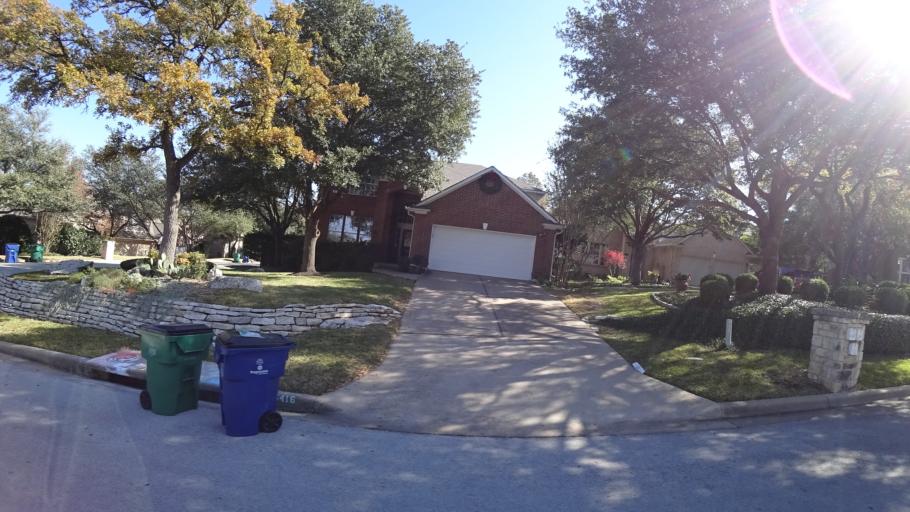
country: US
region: Texas
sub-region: Travis County
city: Lost Creek
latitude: 30.3773
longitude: -97.8472
